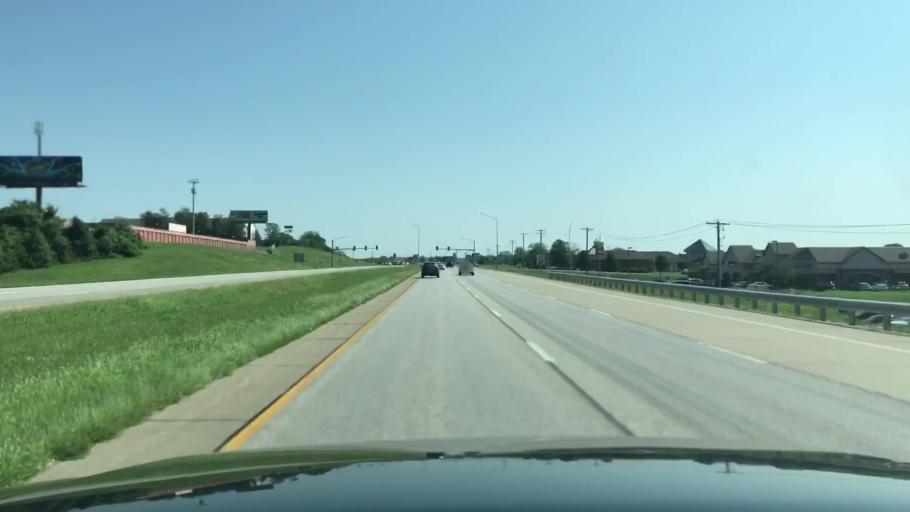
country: US
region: Missouri
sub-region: Saint Charles County
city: Saint Charles
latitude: 38.7582
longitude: -90.5379
